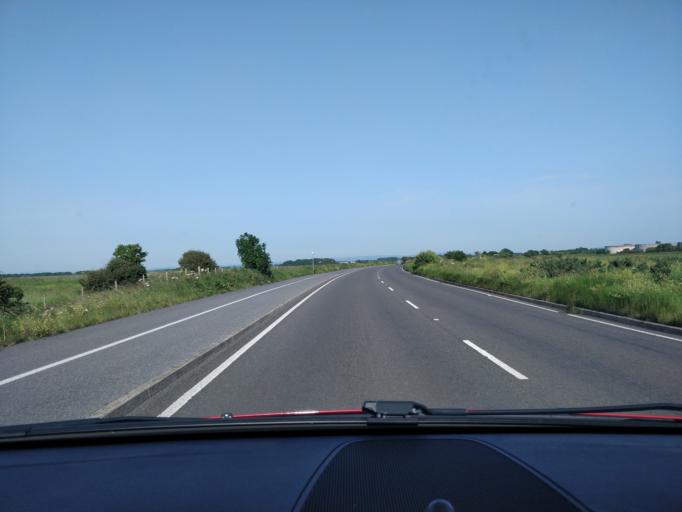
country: GB
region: England
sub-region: Lancashire
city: Banks
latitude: 53.6832
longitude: -2.9626
